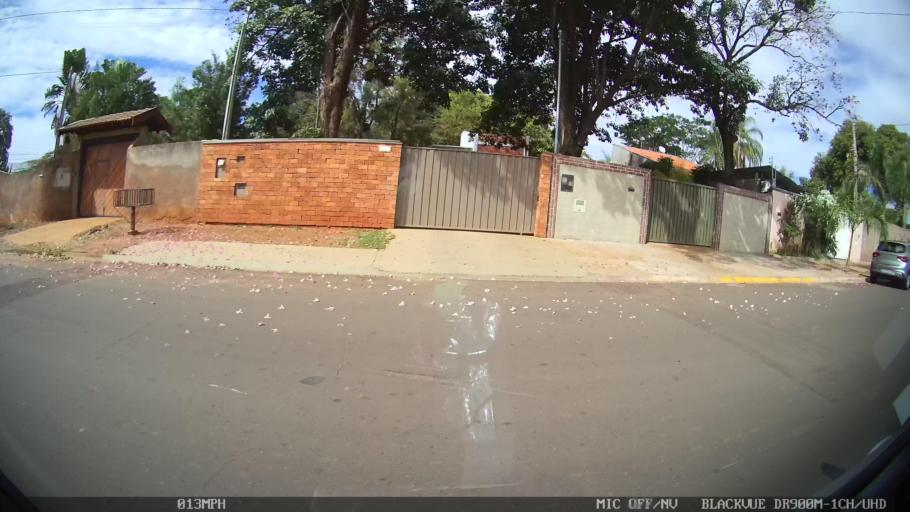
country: BR
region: Sao Paulo
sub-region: Catanduva
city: Catanduva
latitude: -21.1572
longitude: -48.9781
